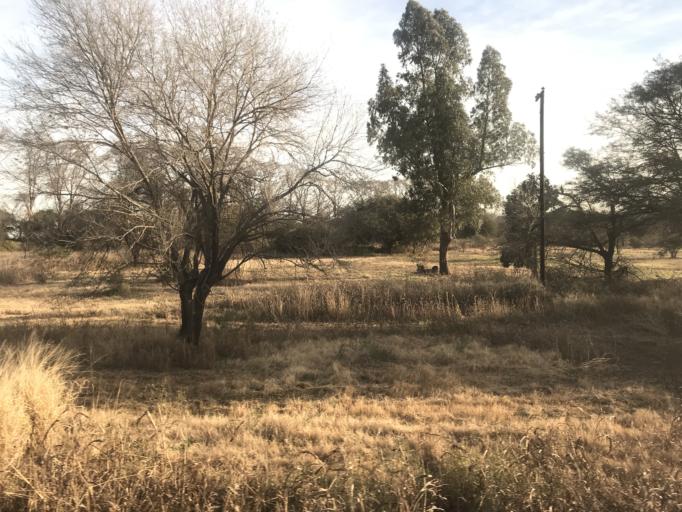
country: AR
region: Cordoba
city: Malvinas Argentinas
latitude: -31.4677
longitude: -64.1003
